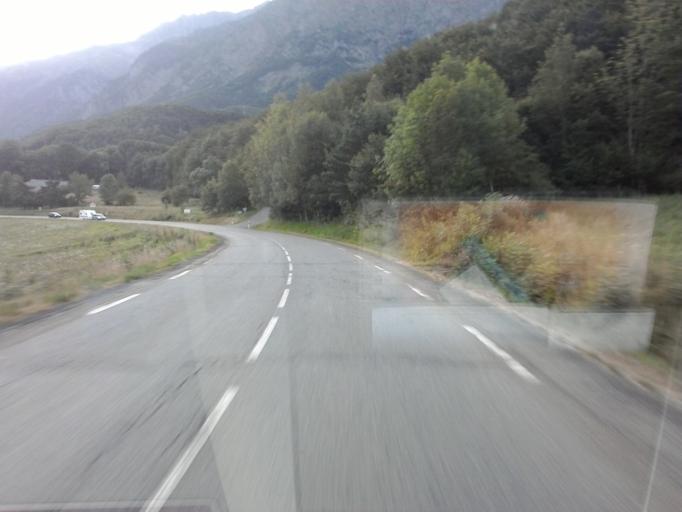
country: FR
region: Provence-Alpes-Cote d'Azur
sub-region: Departement des Hautes-Alpes
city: Saint-Bonnet-en-Champsaur
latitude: 44.7699
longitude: 6.0212
